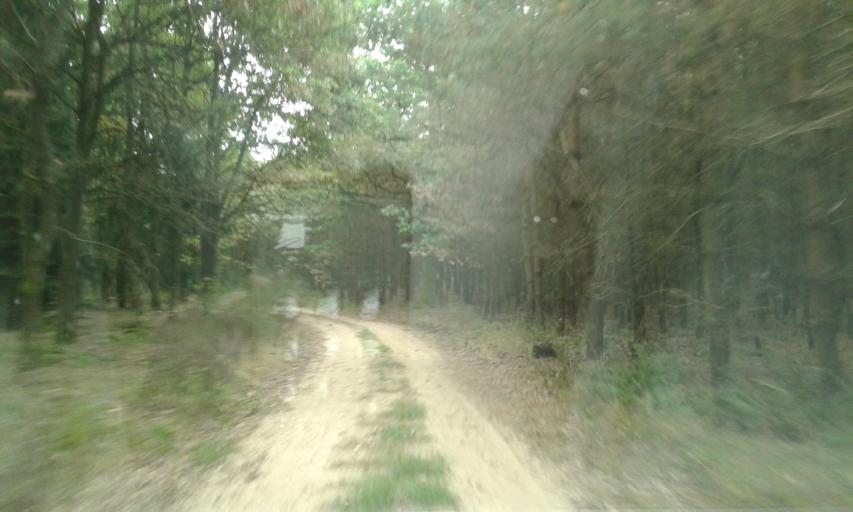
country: PL
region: West Pomeranian Voivodeship
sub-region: Powiat stargardzki
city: Dolice
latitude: 53.1748
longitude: 15.1353
